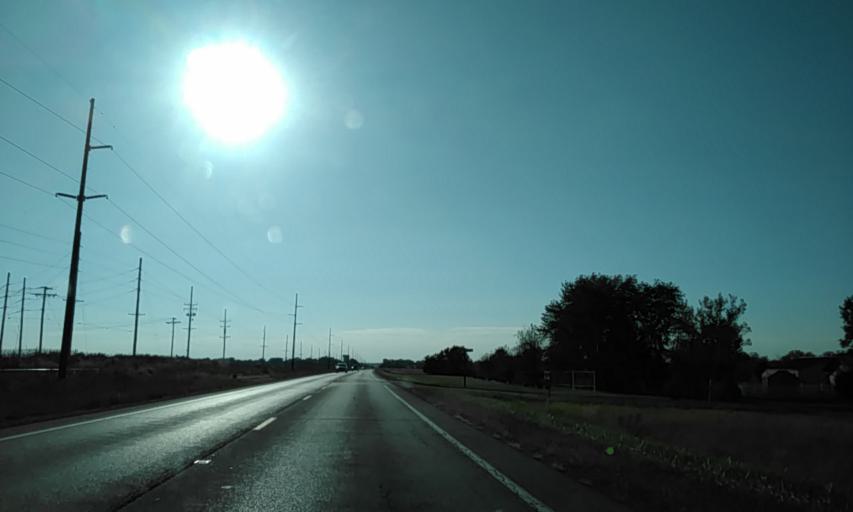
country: US
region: Illinois
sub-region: Madison County
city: Saint Jacob
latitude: 38.7254
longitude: -89.7445
